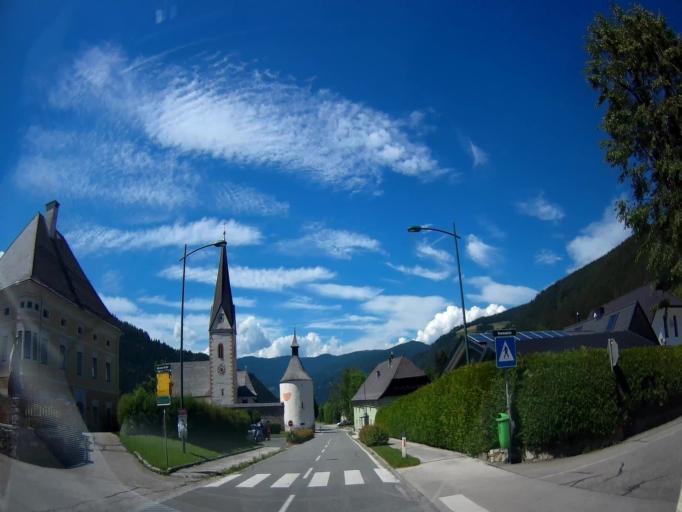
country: AT
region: Carinthia
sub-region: Politischer Bezirk Sankt Veit an der Glan
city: Glodnitz
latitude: 46.8741
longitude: 14.1185
